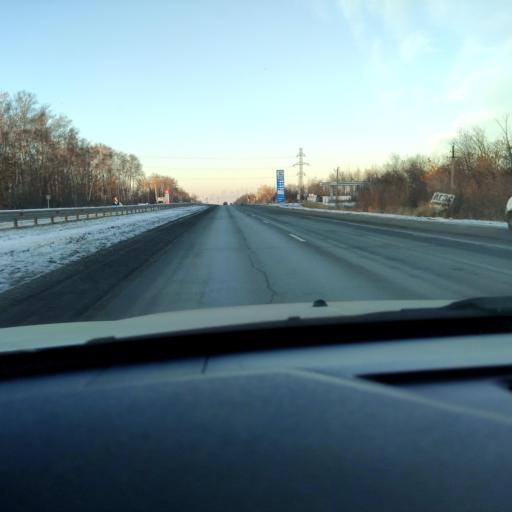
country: RU
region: Samara
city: Smyshlyayevka
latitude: 53.2603
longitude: 50.4642
